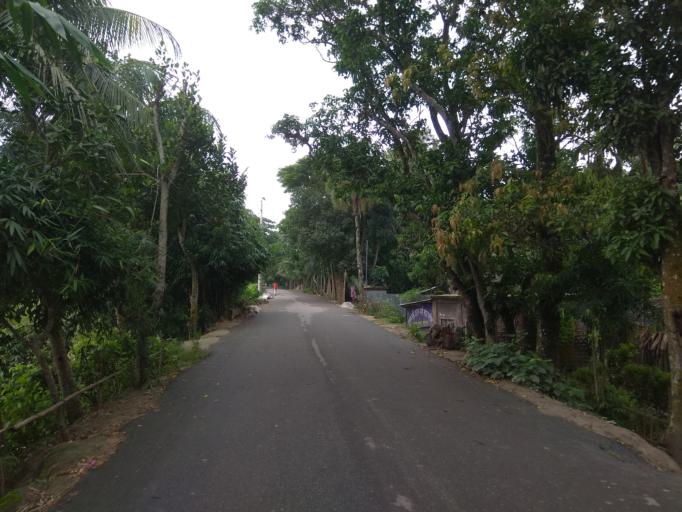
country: BD
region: Dhaka
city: Dohar
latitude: 23.4205
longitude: 90.0666
